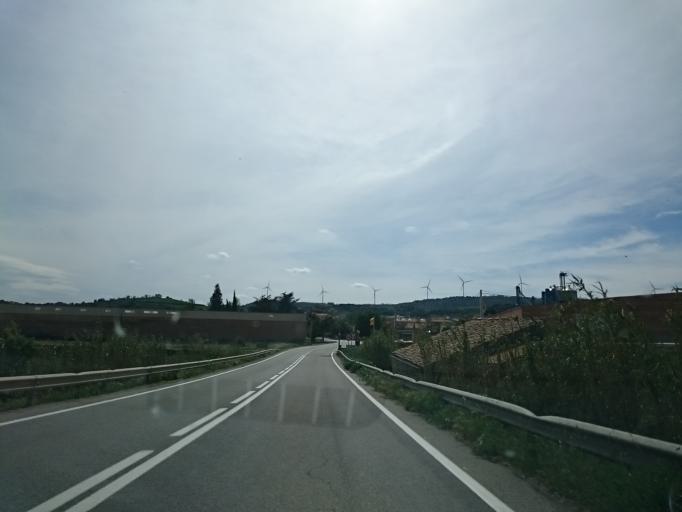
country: ES
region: Catalonia
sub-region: Provincia de Barcelona
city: Calaf
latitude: 41.7041
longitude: 1.4953
